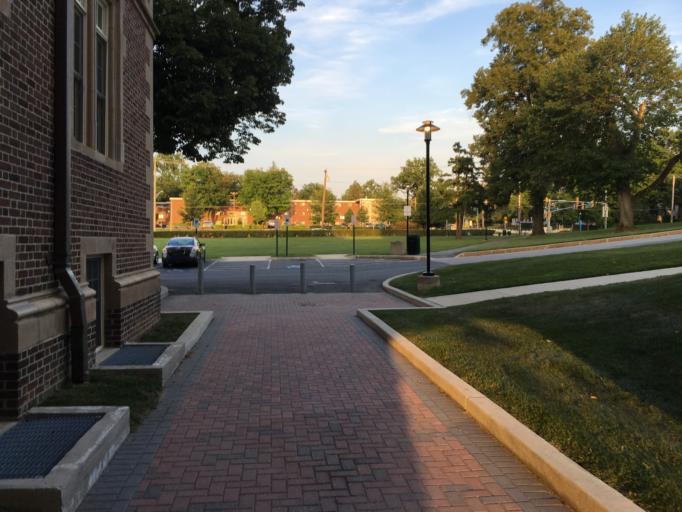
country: US
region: Maryland
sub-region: Baltimore County
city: Towson
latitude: 39.3936
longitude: -76.6056
